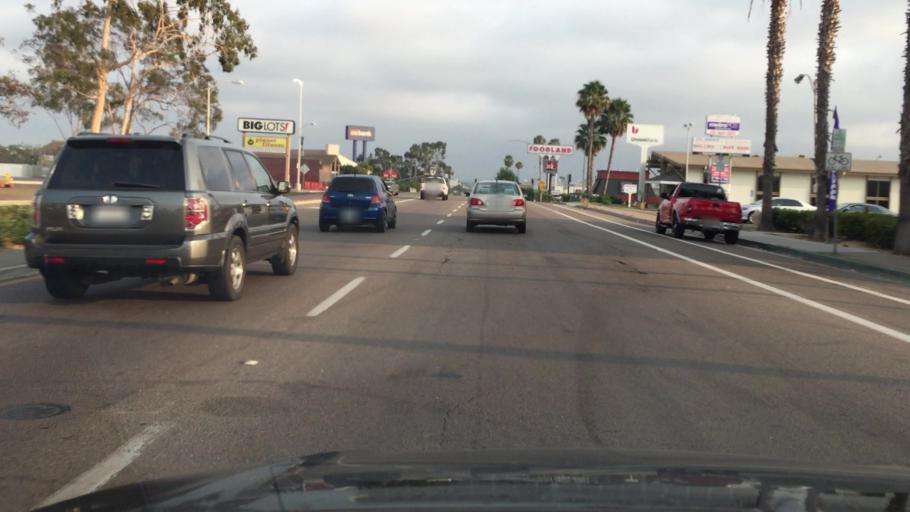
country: US
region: California
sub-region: San Diego County
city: National City
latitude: 32.7235
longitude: -117.0850
